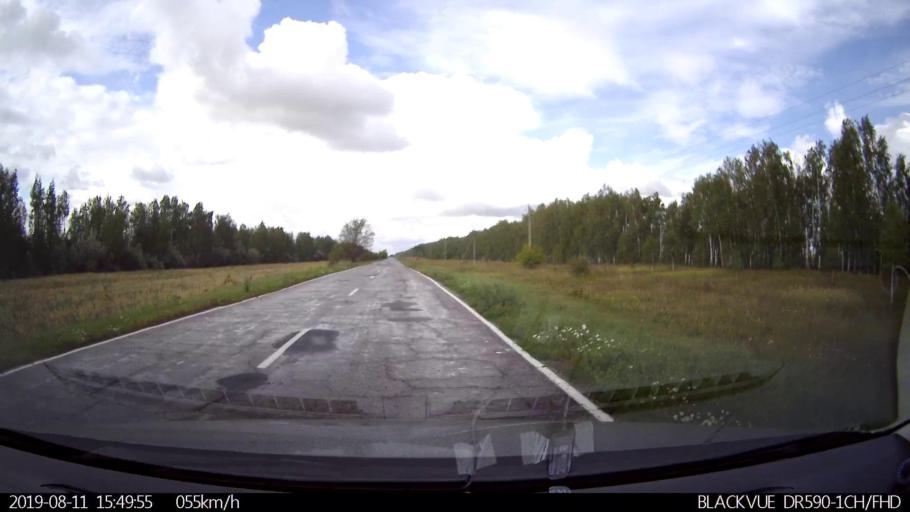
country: RU
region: Ulyanovsk
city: Ignatovka
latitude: 53.9083
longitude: 47.6556
